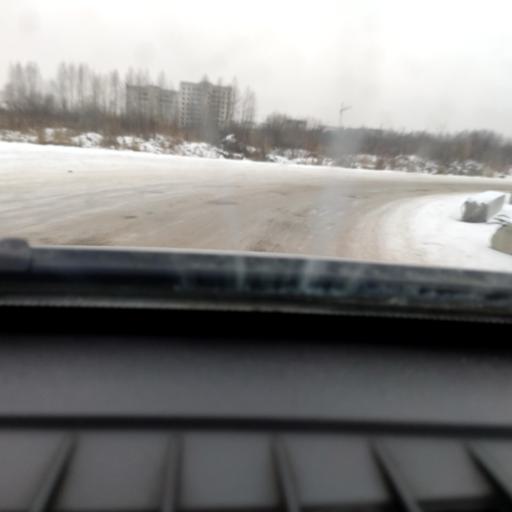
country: RU
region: Perm
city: Perm
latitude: 58.0337
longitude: 56.1937
